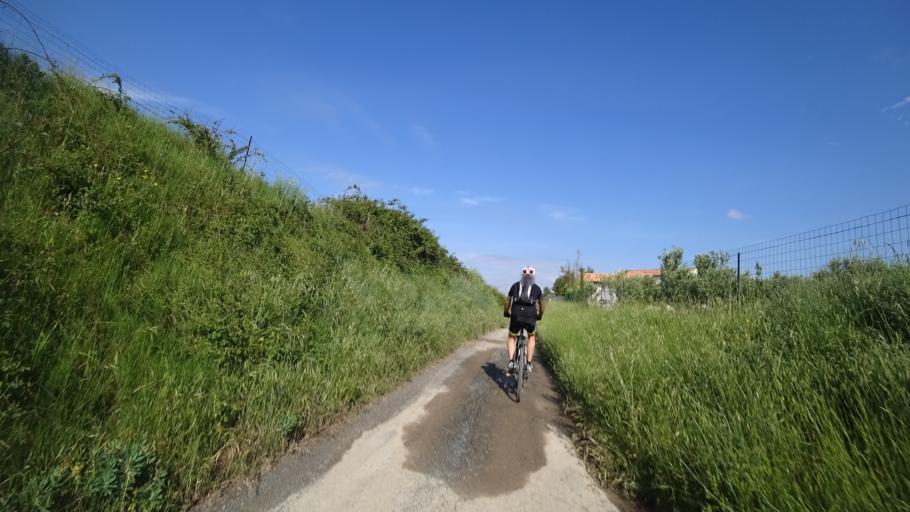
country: FR
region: Languedoc-Roussillon
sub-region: Departement de l'Herault
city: Olonzac
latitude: 43.2529
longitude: 2.7288
